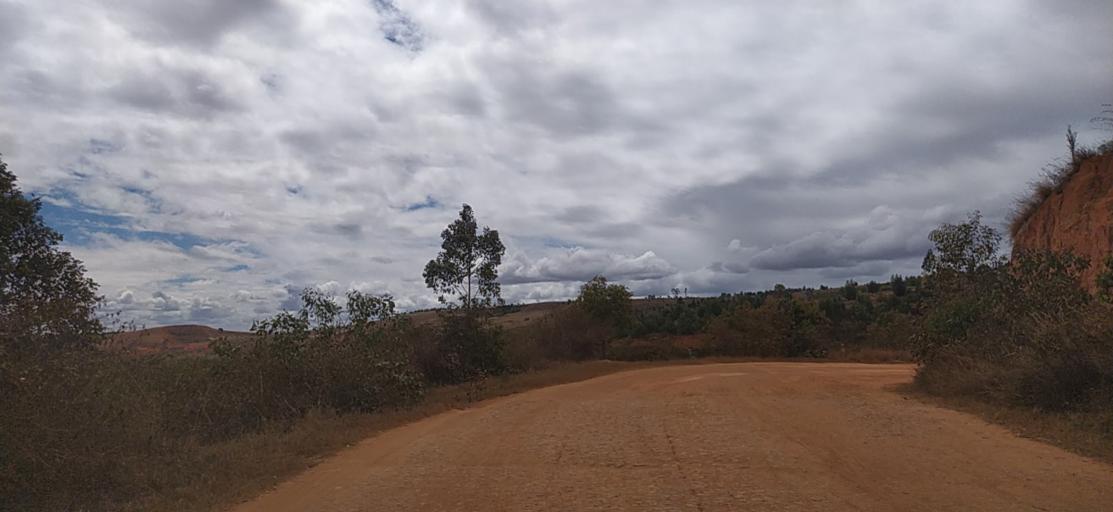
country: MG
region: Alaotra Mangoro
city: Ambatondrazaka
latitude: -18.0017
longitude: 48.2627
